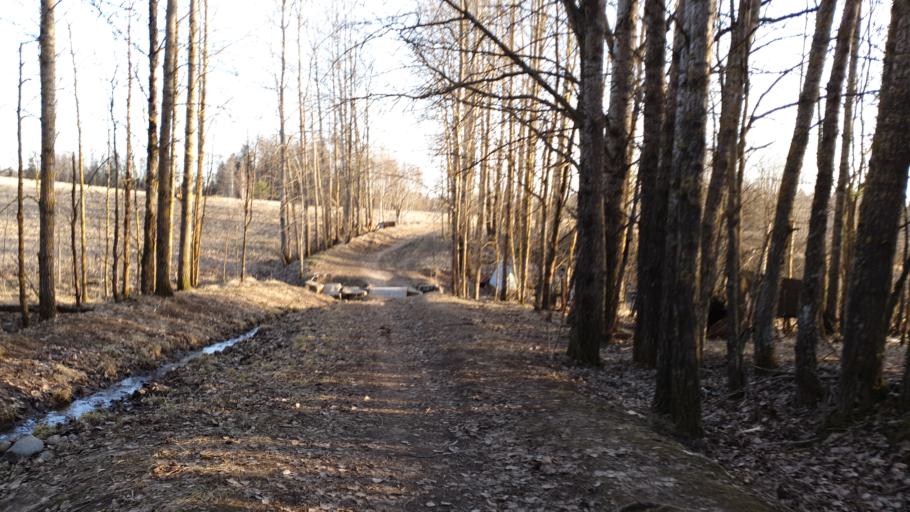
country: FI
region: Uusimaa
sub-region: Helsinki
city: Kilo
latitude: 60.3350
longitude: 24.8432
